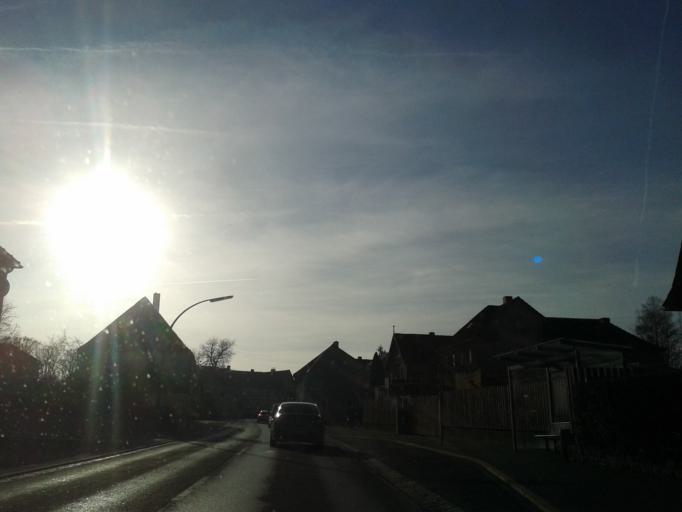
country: DE
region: Bavaria
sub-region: Regierungsbezirk Unterfranken
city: Hassfurt
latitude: 50.0818
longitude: 10.5662
